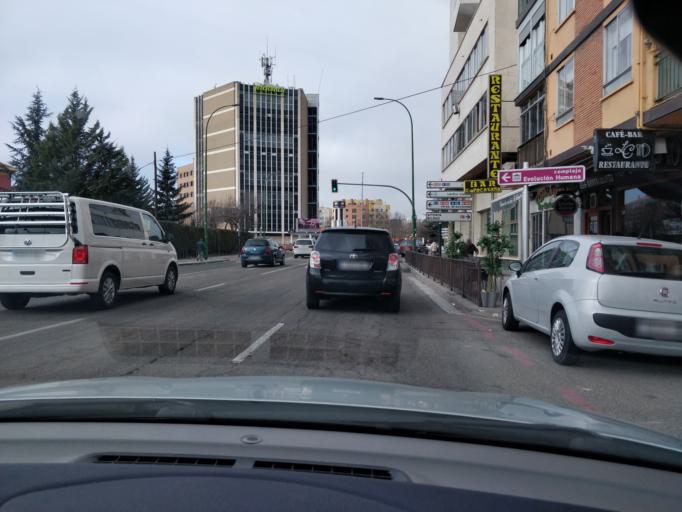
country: ES
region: Castille and Leon
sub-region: Provincia de Burgos
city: Burgos
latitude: 42.3486
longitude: -3.6763
